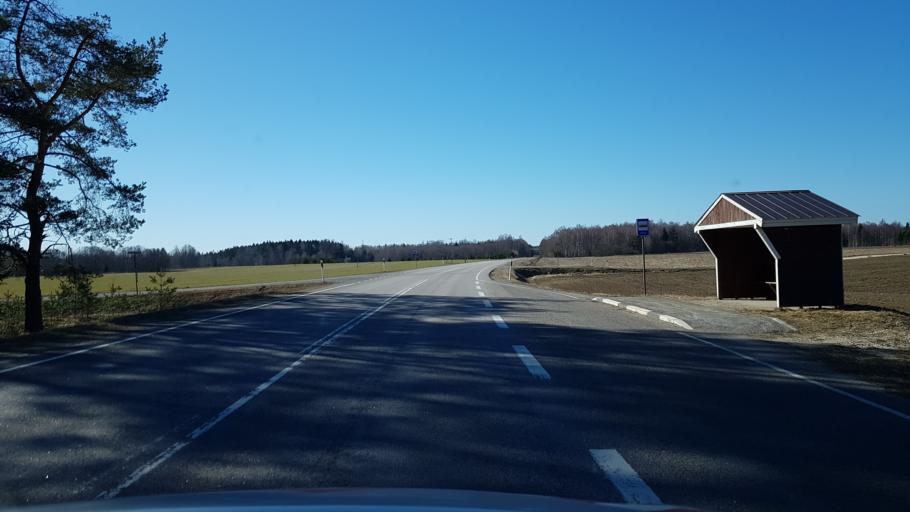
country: EE
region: Laeaene-Virumaa
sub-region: Viru-Nigula vald
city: Kunda
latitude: 59.3608
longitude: 26.6256
